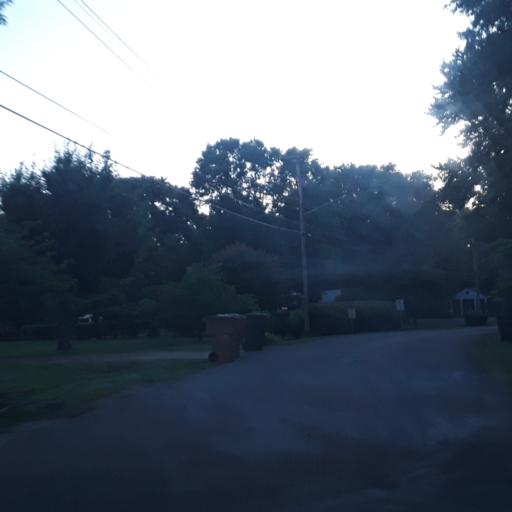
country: US
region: Tennessee
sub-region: Davidson County
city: Oak Hill
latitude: 36.0703
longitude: -86.7661
